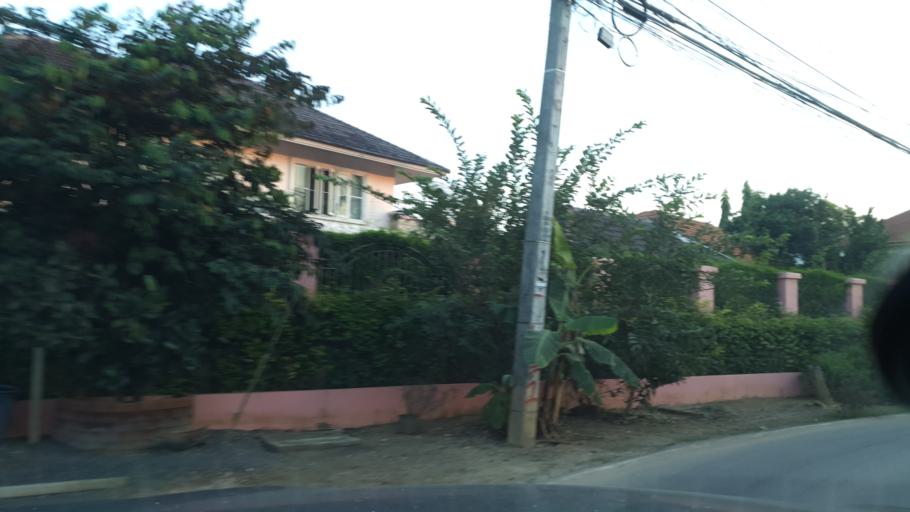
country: TH
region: Chiang Mai
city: San Sai
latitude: 18.8486
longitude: 99.0726
